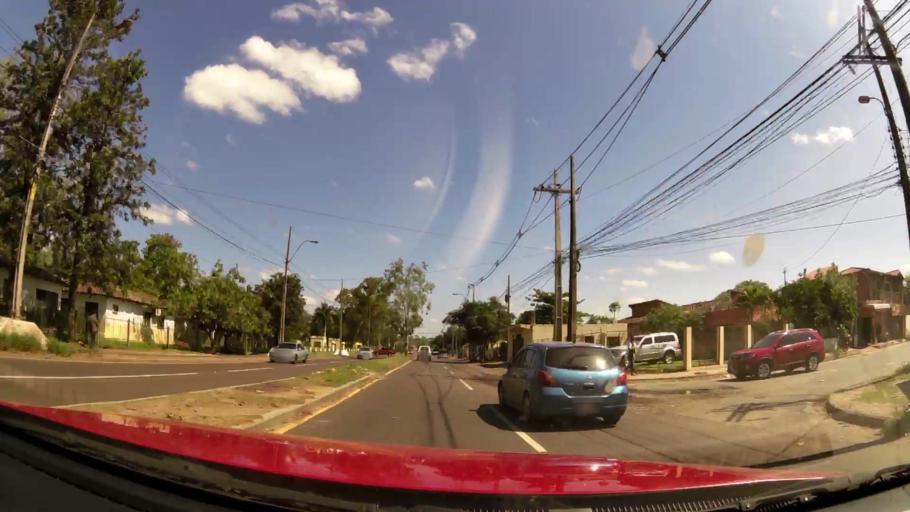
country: PY
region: Central
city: Colonia Mariano Roque Alonso
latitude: -25.2514
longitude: -57.5507
